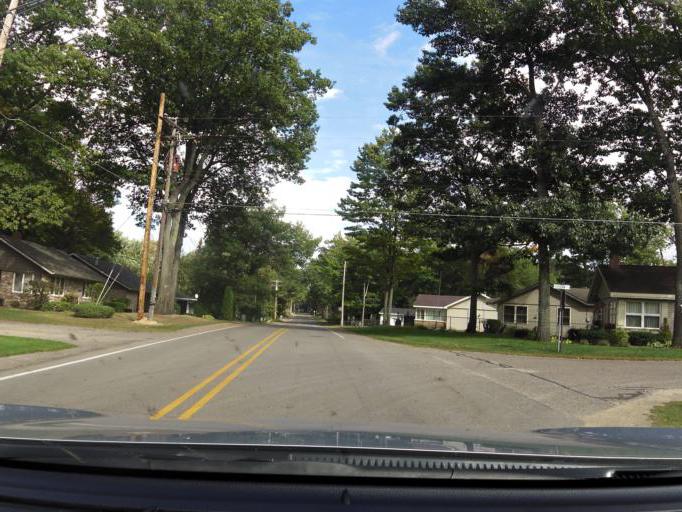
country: US
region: Michigan
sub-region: Roscommon County
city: Houghton Lake
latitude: 44.2999
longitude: -84.7102
